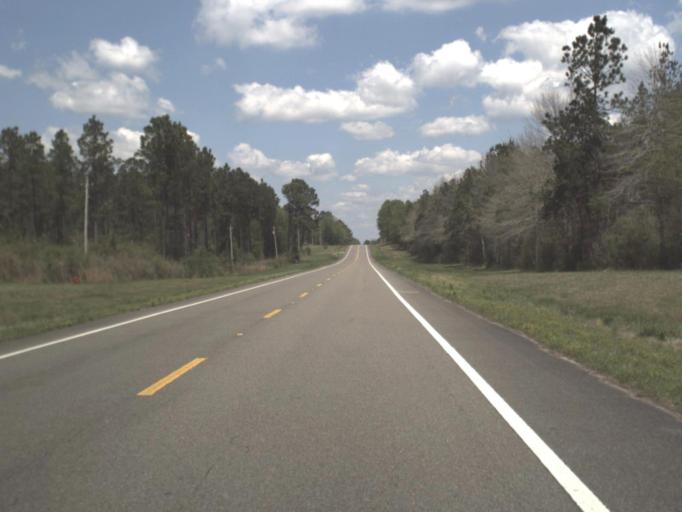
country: US
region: Florida
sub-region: Okaloosa County
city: Crestview
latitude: 30.9369
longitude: -86.6351
